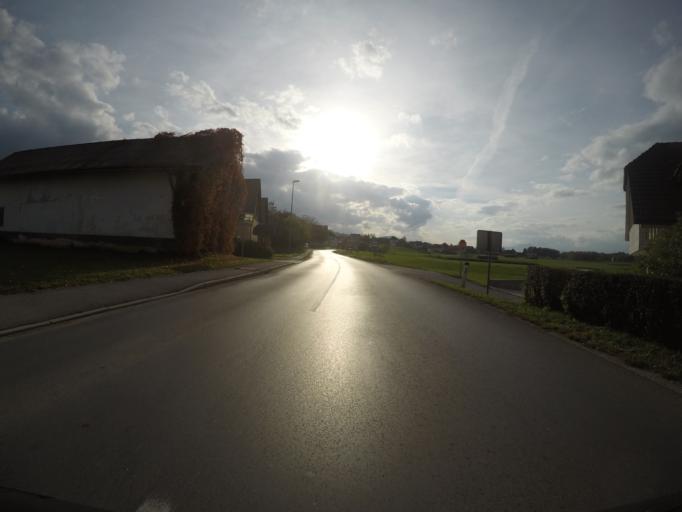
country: SI
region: Medvode
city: Zgornje Pirnice
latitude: 46.1758
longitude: 14.4545
